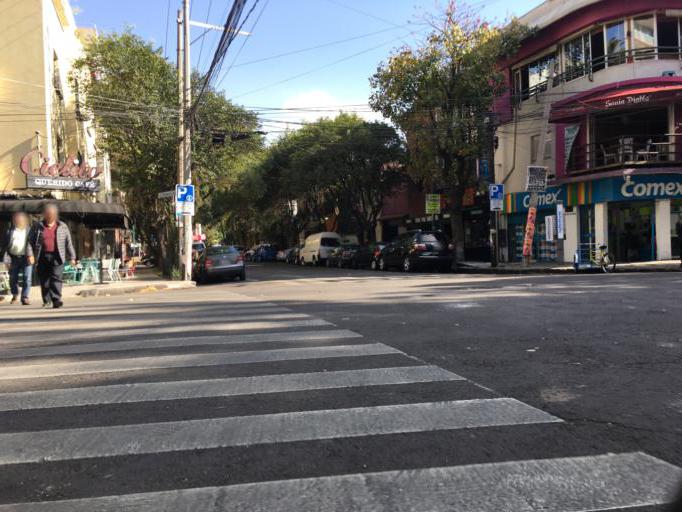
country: MX
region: Mexico City
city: Benito Juarez
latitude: 19.4124
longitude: -99.1733
